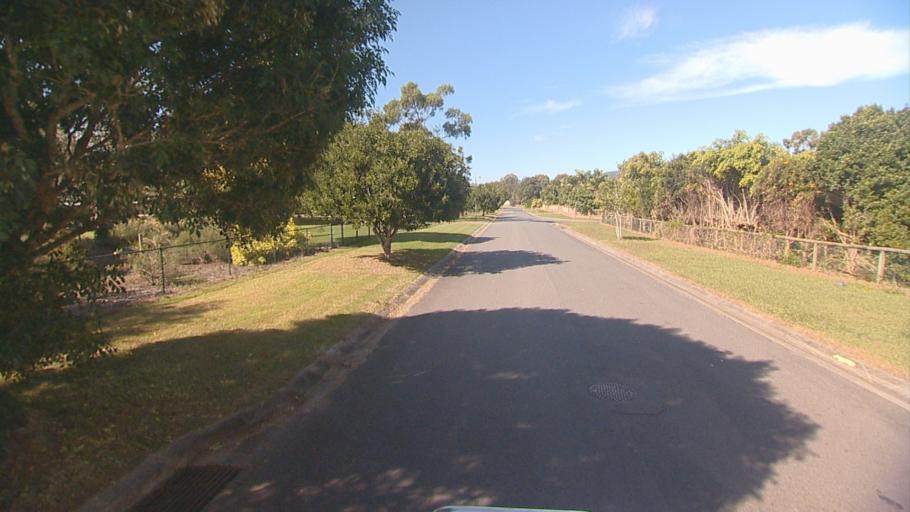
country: AU
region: Queensland
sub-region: Logan
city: Windaroo
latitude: -27.7570
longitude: 153.1783
